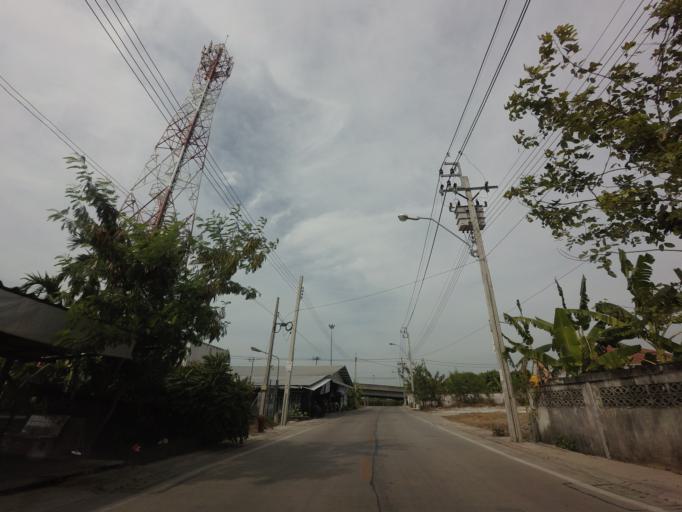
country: TH
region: Bangkok
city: Sai Mai
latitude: 13.8975
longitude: 100.6957
